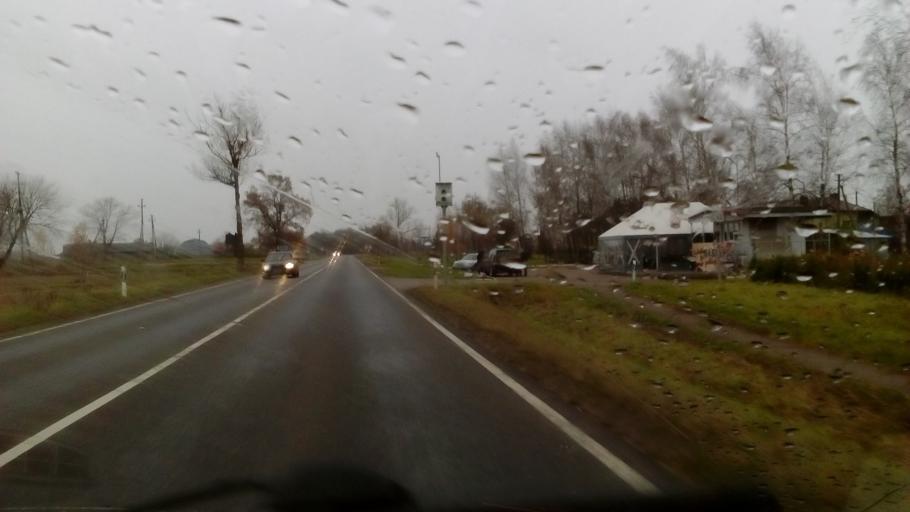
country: LT
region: Marijampoles apskritis
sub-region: Marijampole Municipality
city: Marijampole
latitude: 54.5497
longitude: 23.4037
